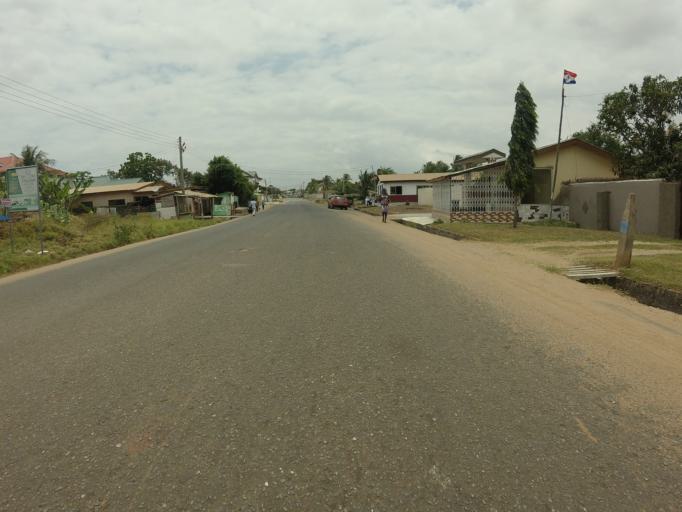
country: GH
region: Greater Accra
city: Nungua
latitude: 5.6178
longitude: -0.0819
